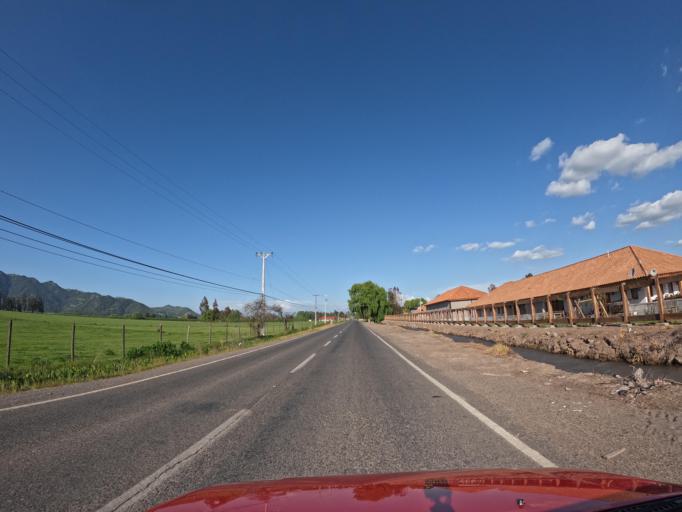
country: CL
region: Maule
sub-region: Provincia de Curico
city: Rauco
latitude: -34.8684
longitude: -71.2525
